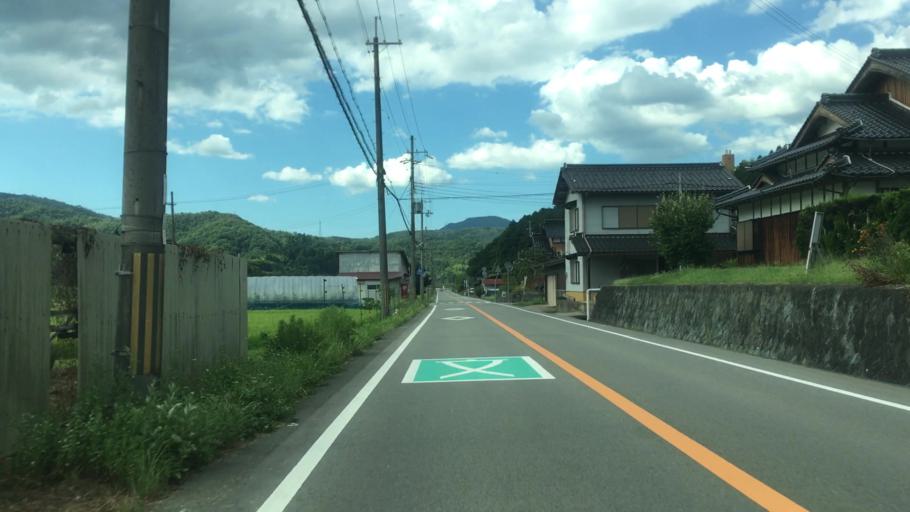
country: JP
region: Hyogo
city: Toyooka
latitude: 35.5421
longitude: 134.7901
